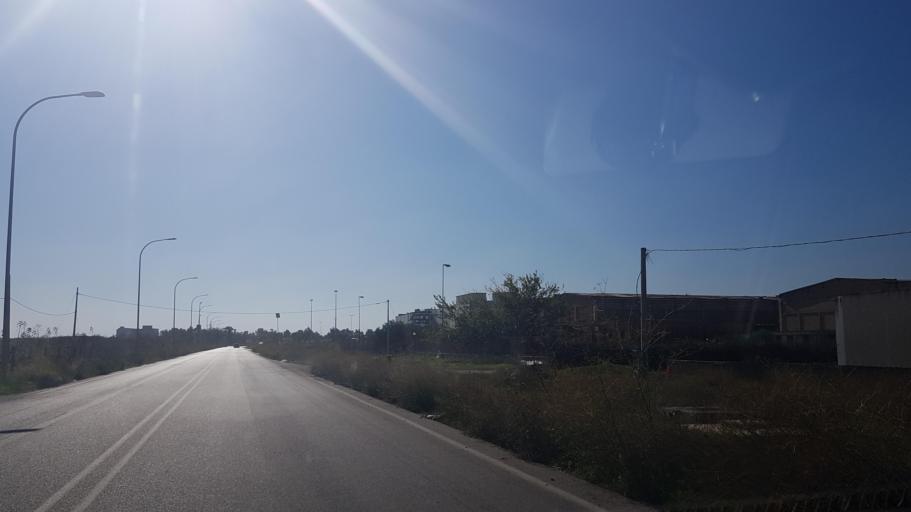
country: IT
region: Apulia
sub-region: Provincia di Foggia
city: Carapelle
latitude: 41.4178
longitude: 15.6554
